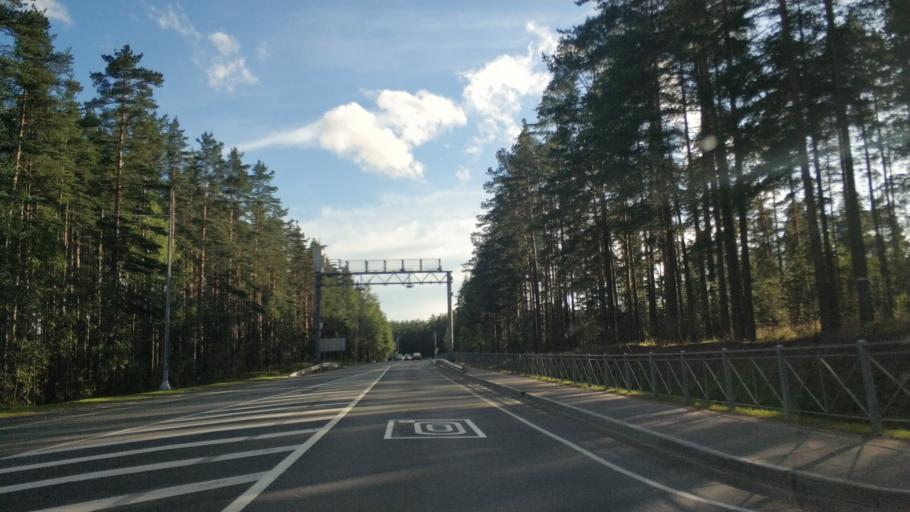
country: RU
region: Leningrad
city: Sapernoye
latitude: 60.7104
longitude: 29.9730
